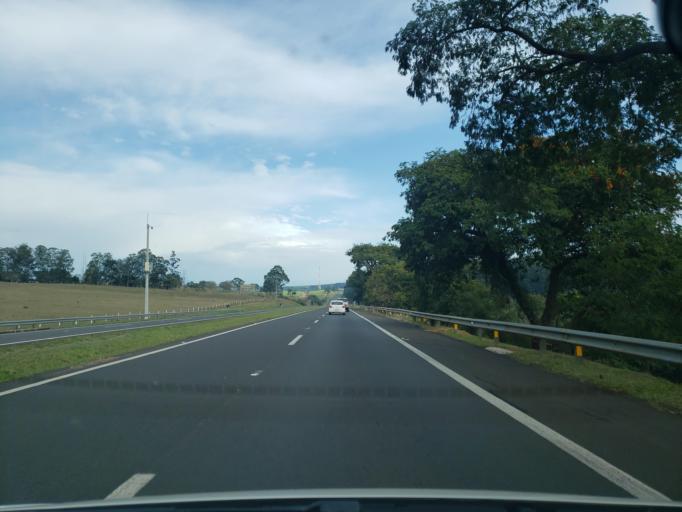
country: BR
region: Sao Paulo
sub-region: Itirapina
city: Itirapina
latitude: -22.2739
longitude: -47.9583
